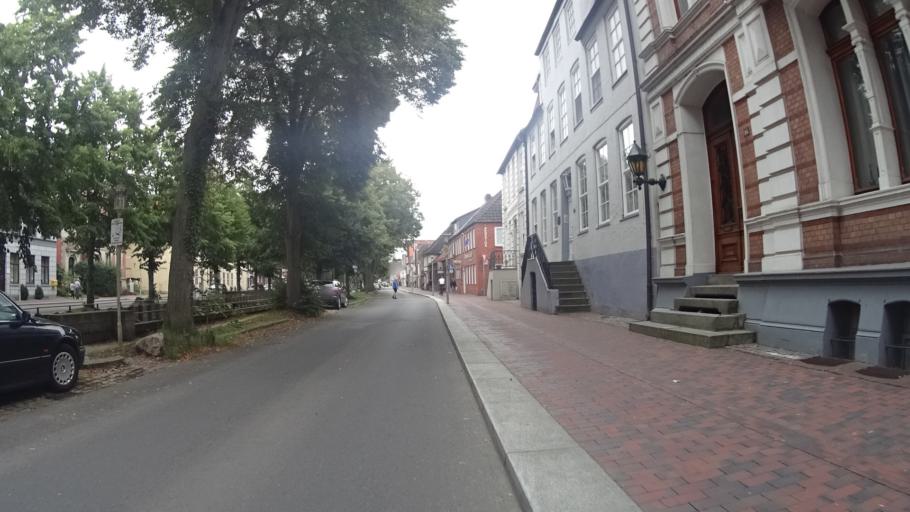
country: DE
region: Schleswig-Holstein
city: Gluckstadt
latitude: 53.7893
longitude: 9.4207
